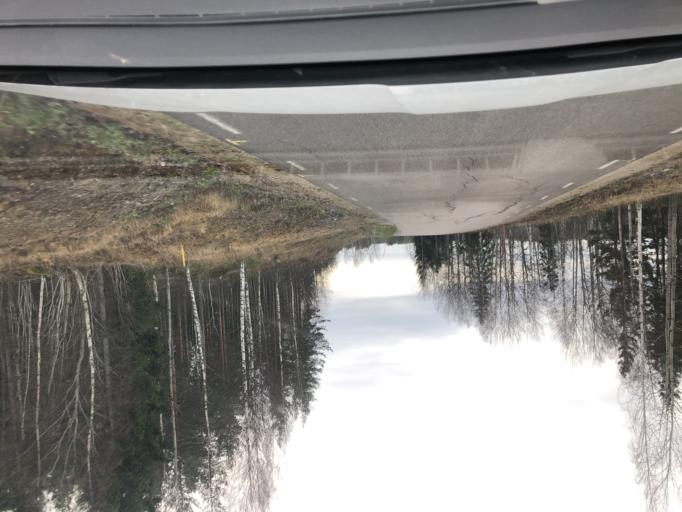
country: SE
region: Gaevleborg
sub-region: Hudiksvalls Kommun
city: Sorforsa
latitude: 61.6657
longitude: 16.9262
